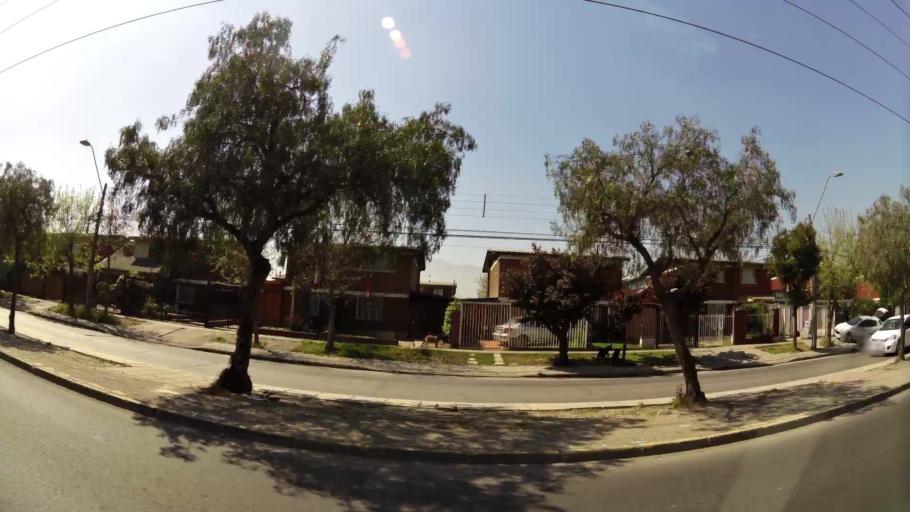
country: CL
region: Santiago Metropolitan
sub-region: Provincia de Santiago
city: La Pintana
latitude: -33.5569
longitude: -70.6012
